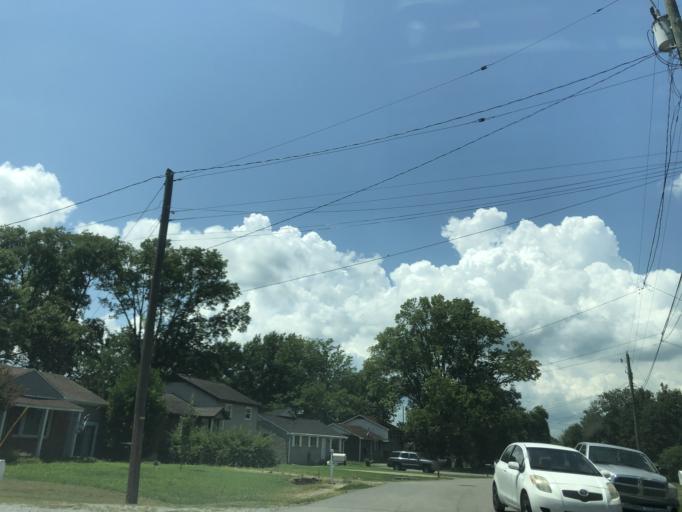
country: US
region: Tennessee
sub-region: Davidson County
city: Lakewood
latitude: 36.1907
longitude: -86.6201
